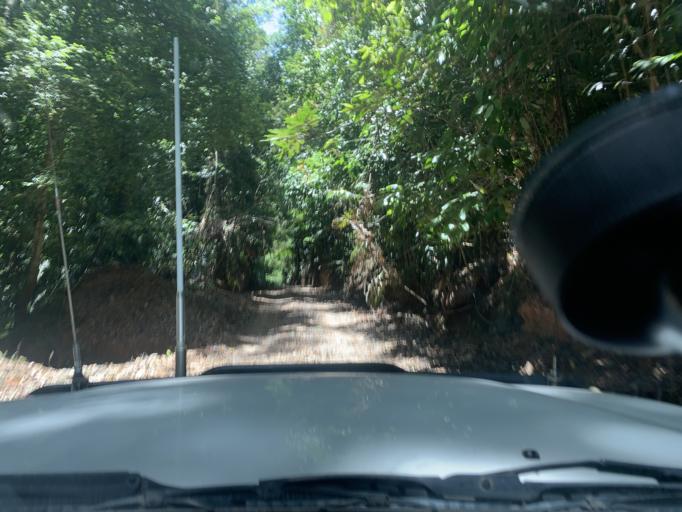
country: AU
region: Queensland
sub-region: Cairns
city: Woree
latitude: -16.9749
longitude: 145.6524
